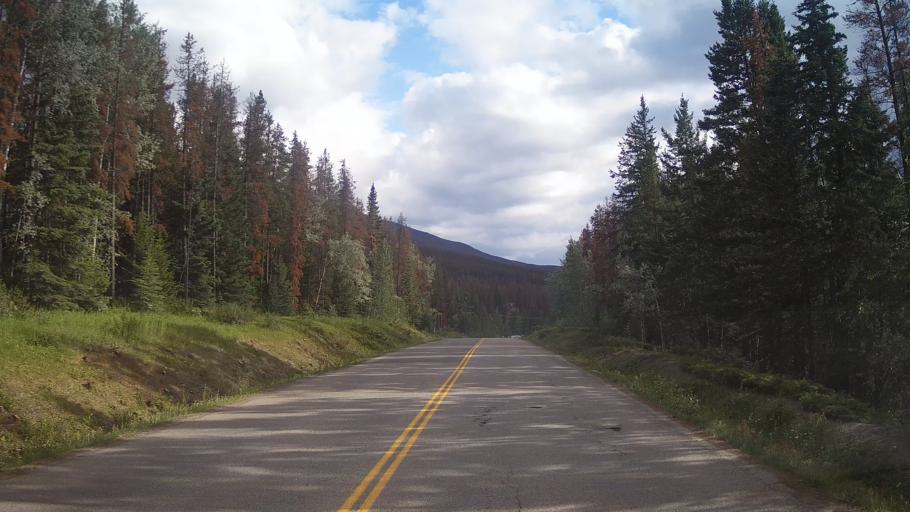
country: CA
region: Alberta
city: Jasper Park Lodge
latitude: 52.9170
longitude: -118.0014
